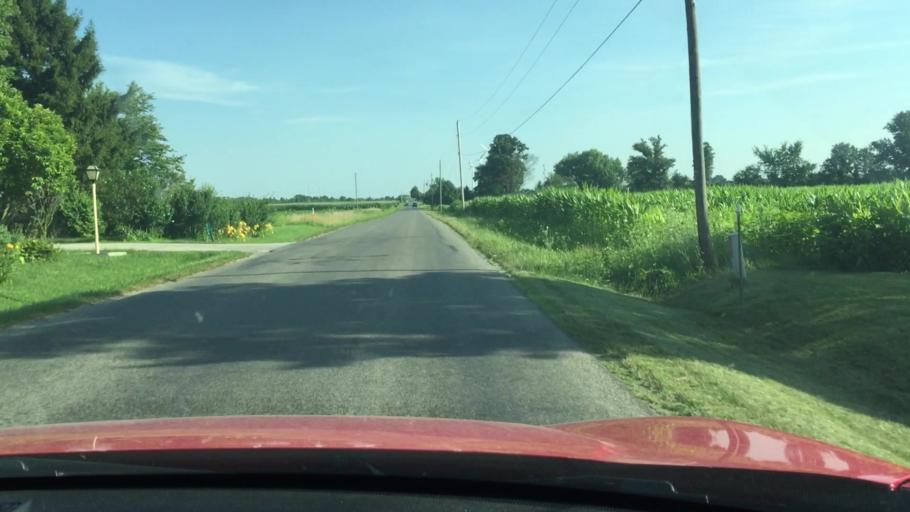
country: US
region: Ohio
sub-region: Hardin County
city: Ada
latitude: 40.7751
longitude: -83.8424
